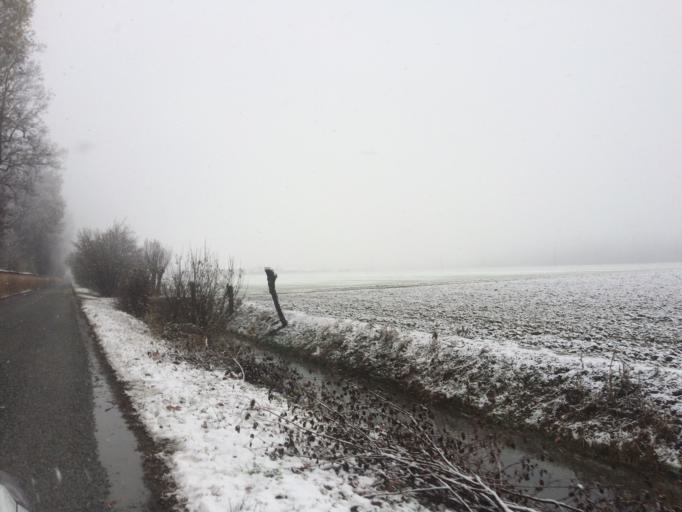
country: IT
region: Piedmont
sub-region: Provincia di Cuneo
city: Racconigi
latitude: 44.7841
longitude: 7.6671
